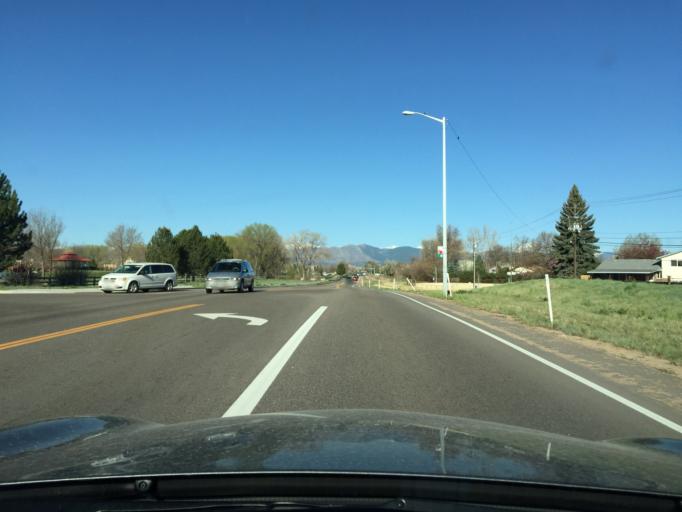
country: US
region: Colorado
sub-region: Boulder County
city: Longmont
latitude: 40.1379
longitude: -105.1150
